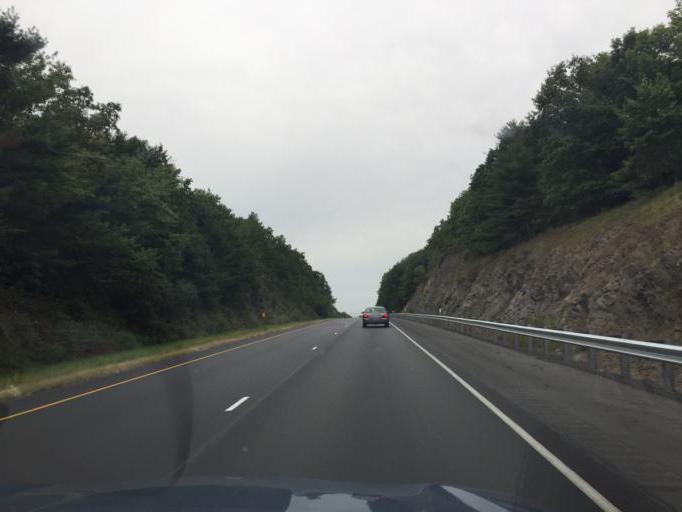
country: US
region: New York
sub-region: Columbia County
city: Niverville
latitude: 42.4837
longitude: -73.6549
